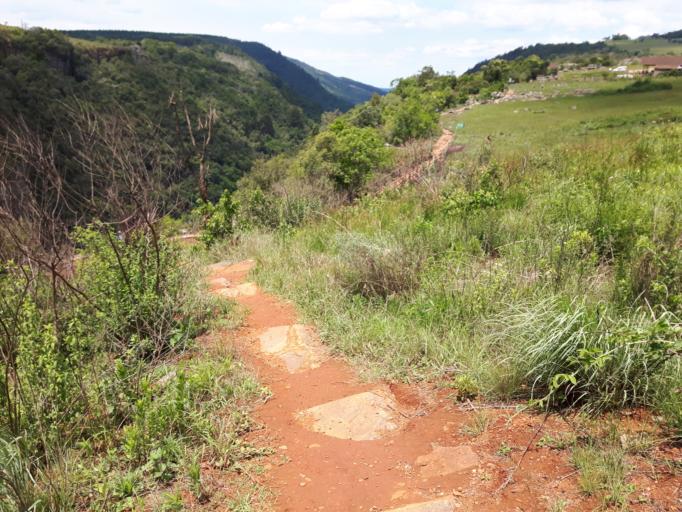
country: ZA
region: Mpumalanga
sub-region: Ehlanzeni District
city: Graksop
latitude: -25.0013
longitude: 30.8177
